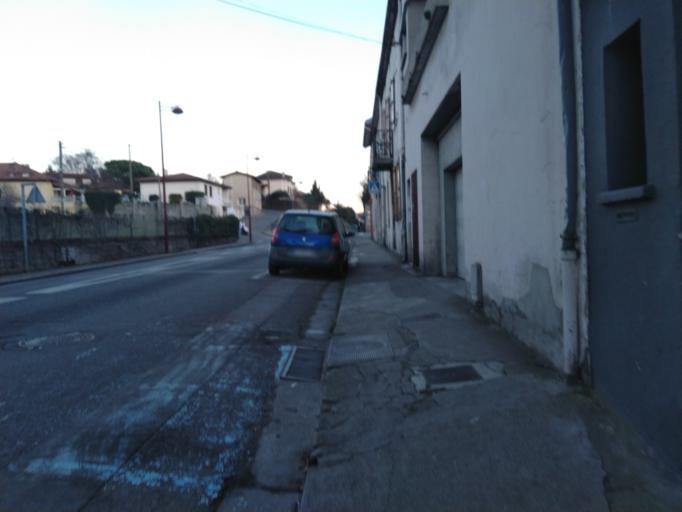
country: FR
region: Midi-Pyrenees
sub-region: Departement de l'Ariege
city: Pamiers
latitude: 43.1105
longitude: 1.6141
